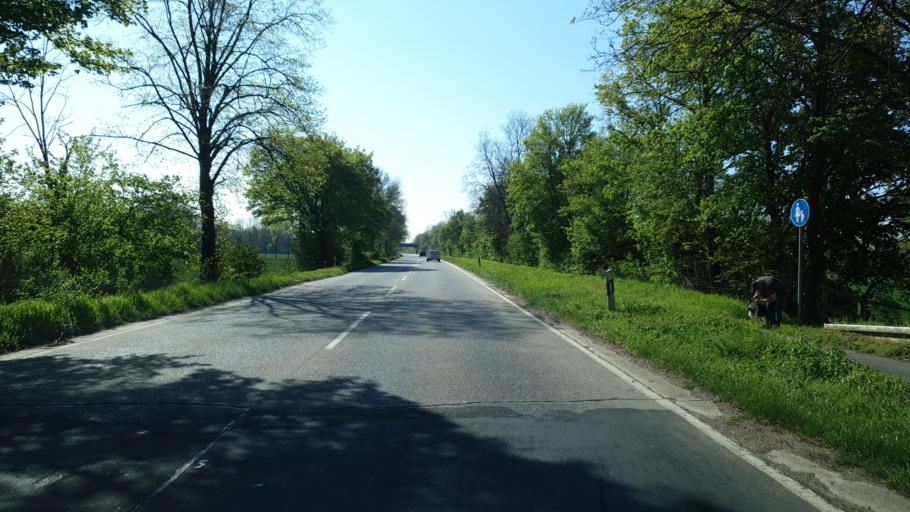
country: DE
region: North Rhine-Westphalia
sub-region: Regierungsbezirk Koln
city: Bergheim
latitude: 50.9255
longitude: 6.6698
